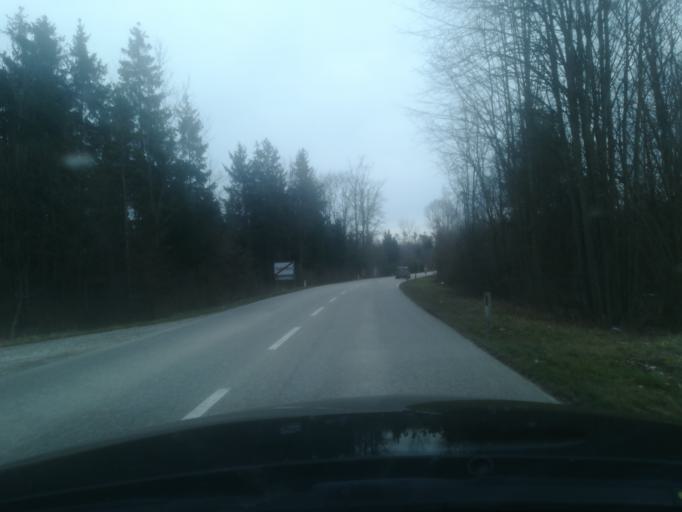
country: AT
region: Upper Austria
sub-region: Wels-Land
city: Lambach
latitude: 48.0817
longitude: 13.8823
